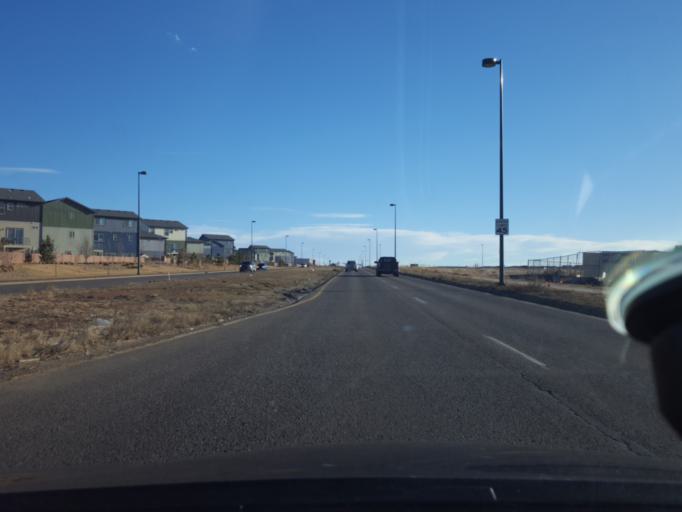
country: US
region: Colorado
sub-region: Adams County
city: Aurora
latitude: 39.7924
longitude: -104.7722
